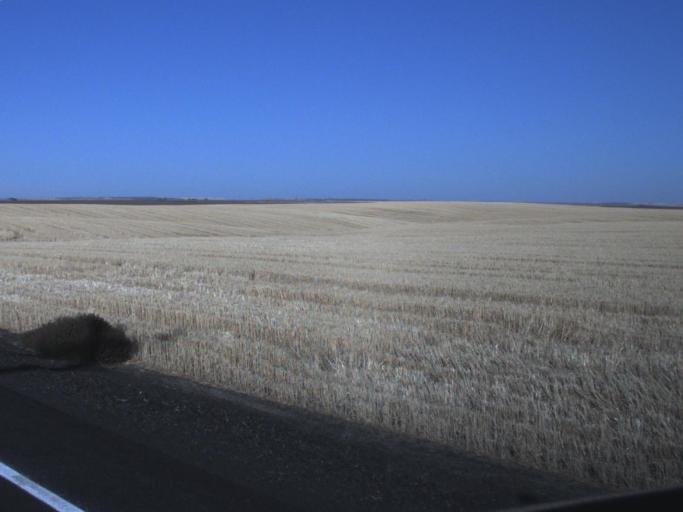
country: US
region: Washington
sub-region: Adams County
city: Ritzville
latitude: 46.8925
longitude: -118.3338
